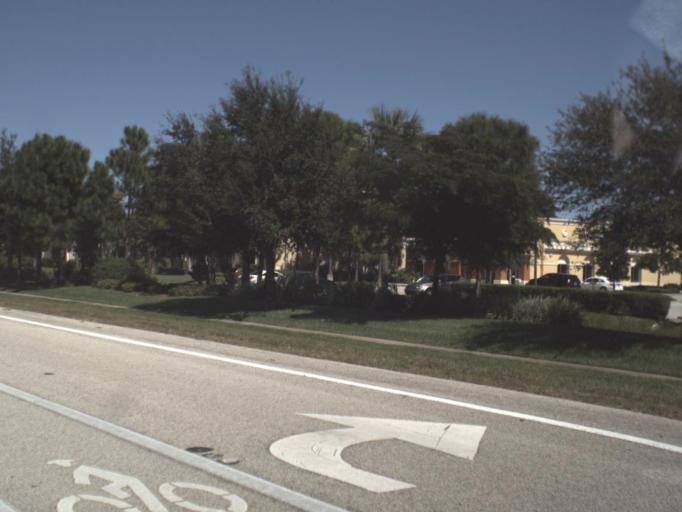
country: US
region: Florida
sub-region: Lee County
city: Estero
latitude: 26.4007
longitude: -81.8105
